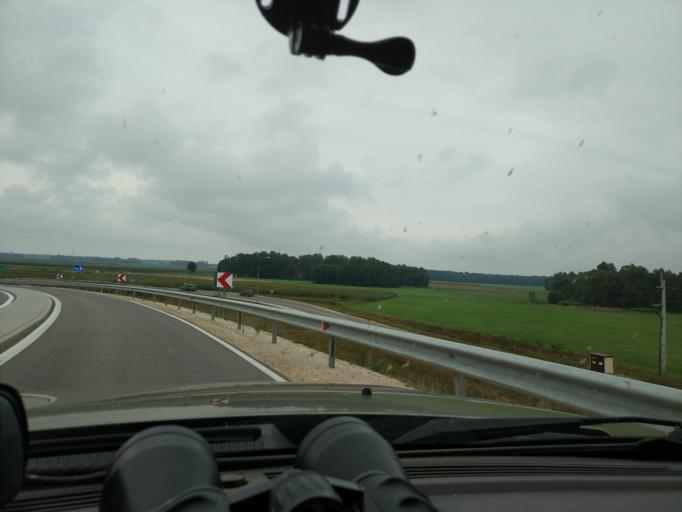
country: PL
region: Podlasie
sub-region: Powiat zambrowski
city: Szumowo
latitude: 52.9100
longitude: 22.1005
